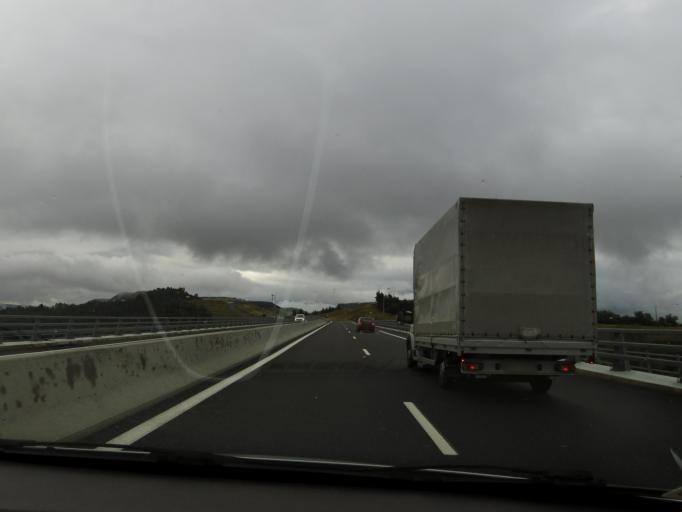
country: FR
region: Languedoc-Roussillon
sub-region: Departement de la Lozere
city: Chirac
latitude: 44.4987
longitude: 3.2505
